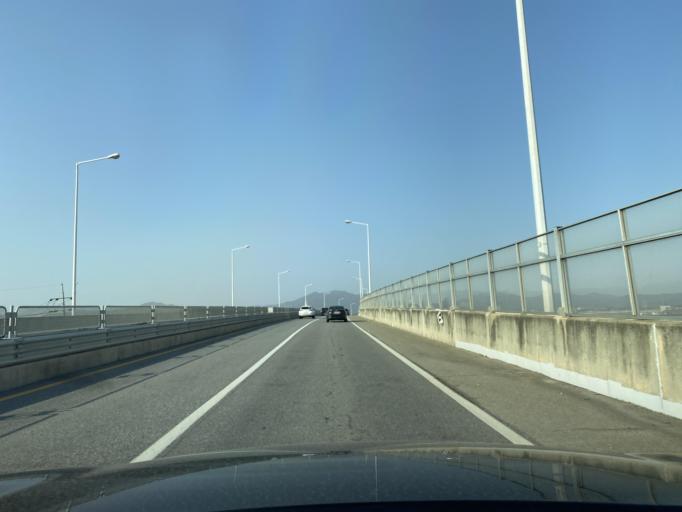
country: KR
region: Chungcheongnam-do
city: Yesan
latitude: 36.6912
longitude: 126.7397
